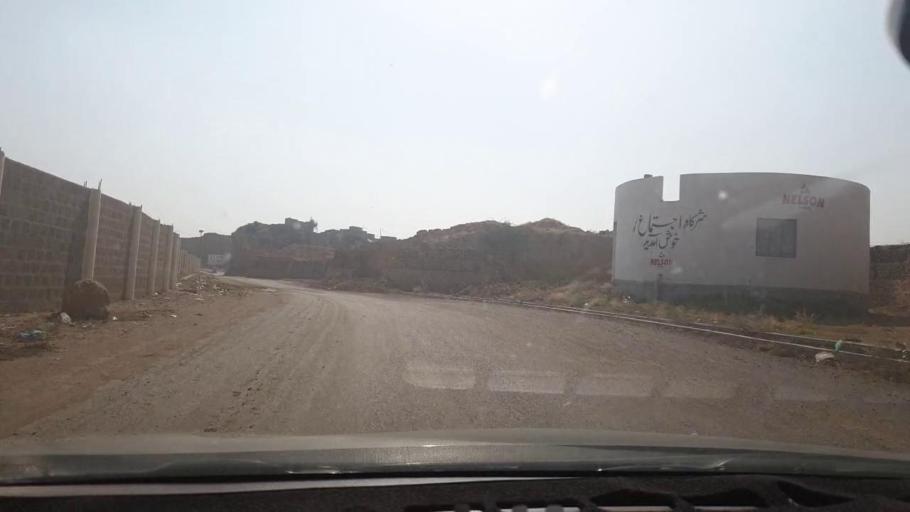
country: PK
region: Sindh
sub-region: Karachi District
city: Karachi
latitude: 24.9706
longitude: 66.9980
